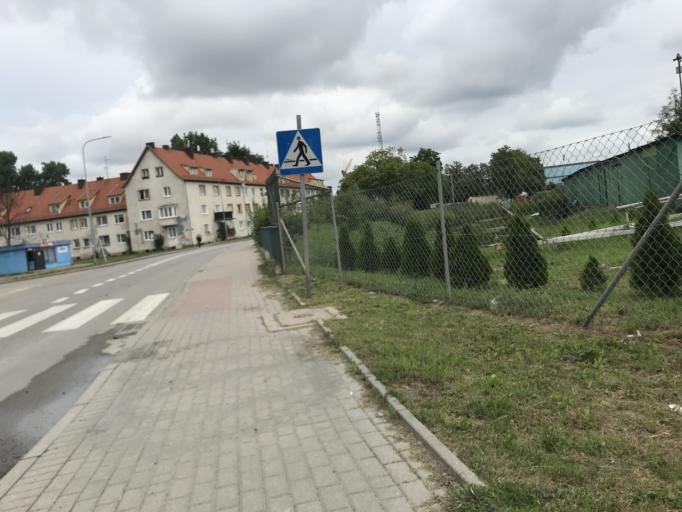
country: PL
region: Warmian-Masurian Voivodeship
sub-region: Powiat elblaski
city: Elblag
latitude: 54.1609
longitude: 19.3895
